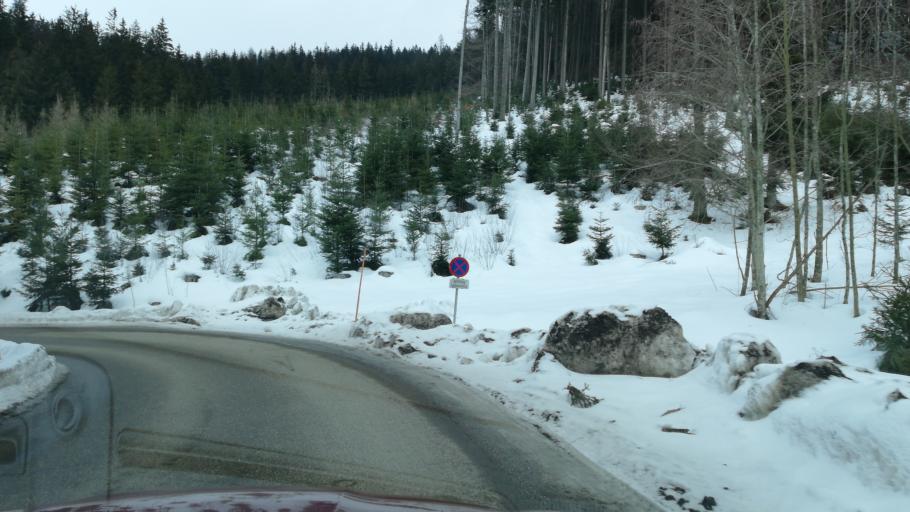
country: AT
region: Upper Austria
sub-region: Politischer Bezirk Vocklabruck
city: Wolfsegg am Hausruck
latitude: 48.1454
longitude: 13.6025
